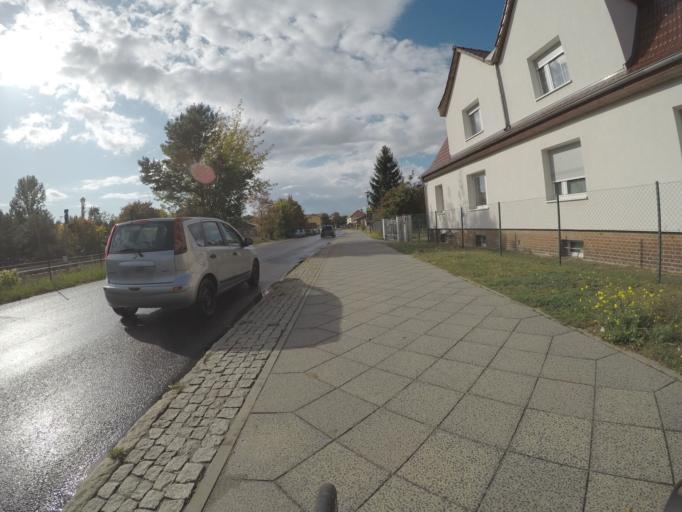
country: DE
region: Brandenburg
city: Petershagen
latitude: 52.5321
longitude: 13.8387
